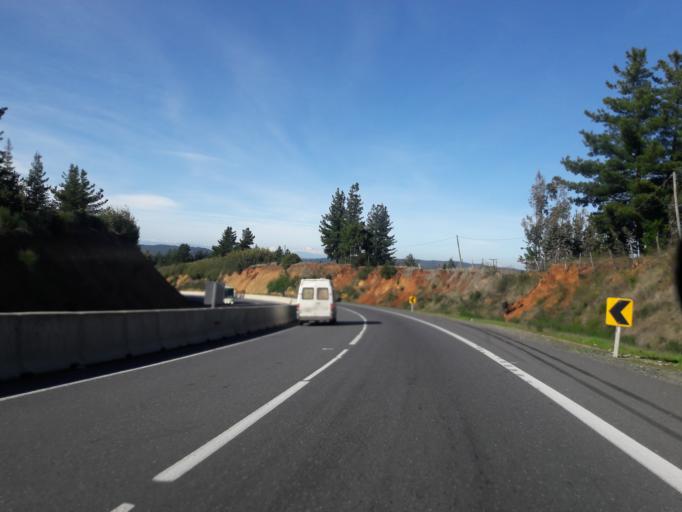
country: CL
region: Biobio
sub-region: Provincia de Biobio
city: Yumbel
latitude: -36.9775
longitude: -72.6509
